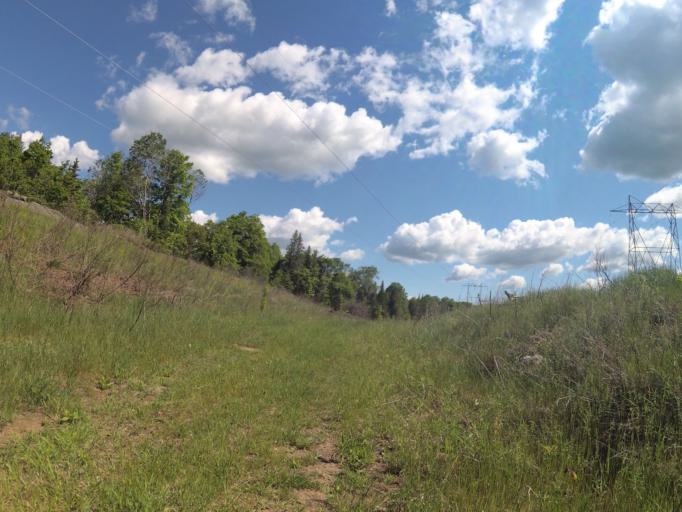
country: CA
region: Ontario
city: Renfrew
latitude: 45.0467
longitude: -76.7654
